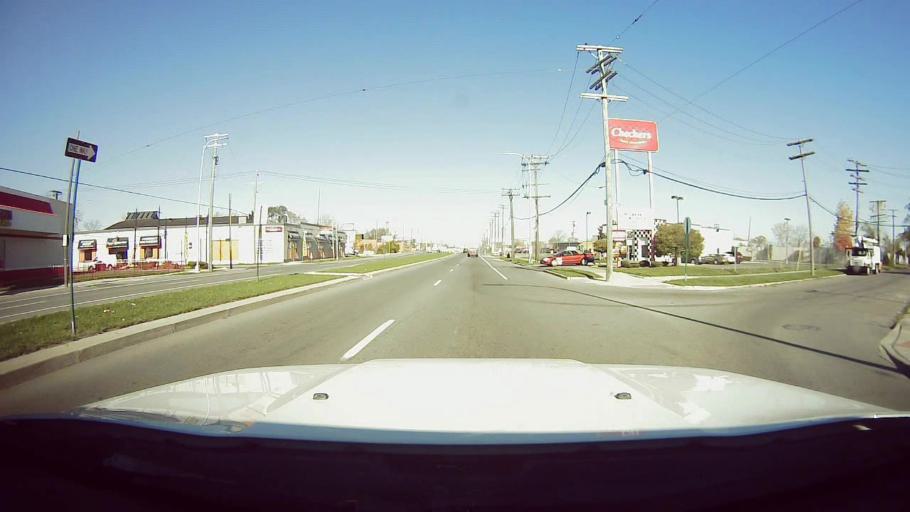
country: US
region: Michigan
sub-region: Wayne County
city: Highland Park
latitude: 42.3933
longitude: -83.1397
